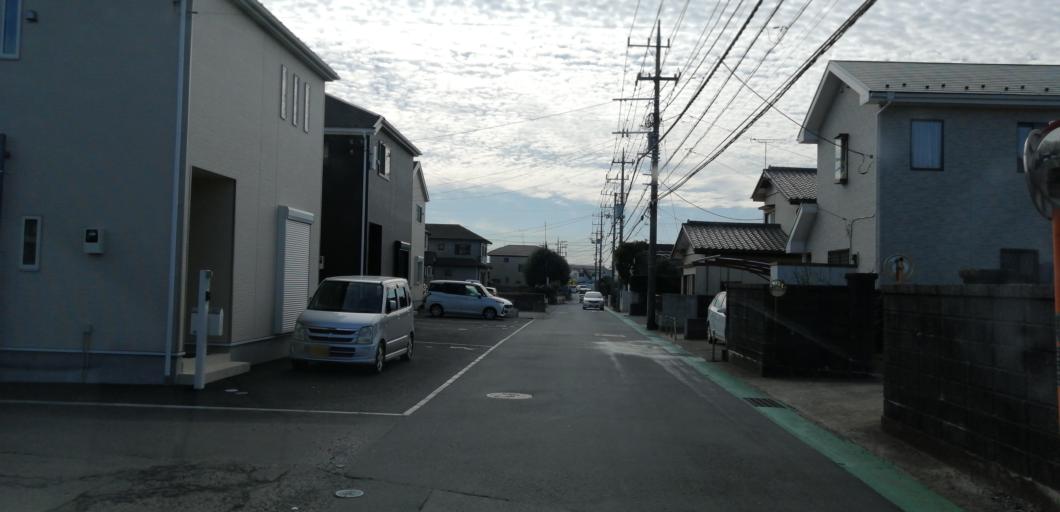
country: JP
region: Chiba
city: Narita
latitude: 35.7415
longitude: 140.3320
